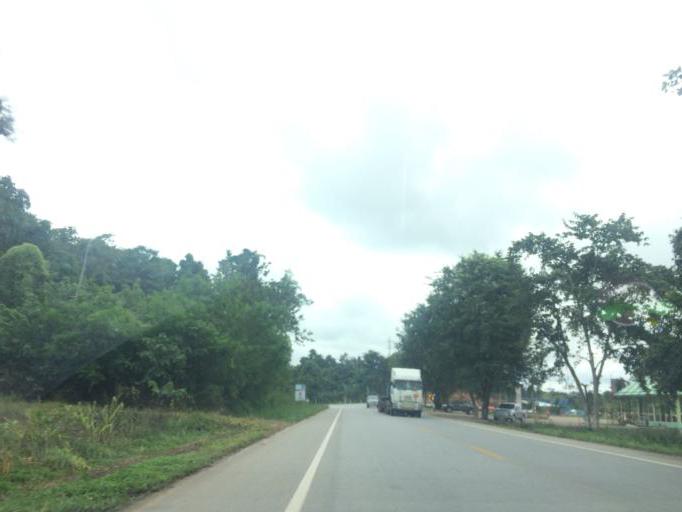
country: TH
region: Chiang Rai
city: Mae Lao
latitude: 19.7466
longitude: 99.6837
